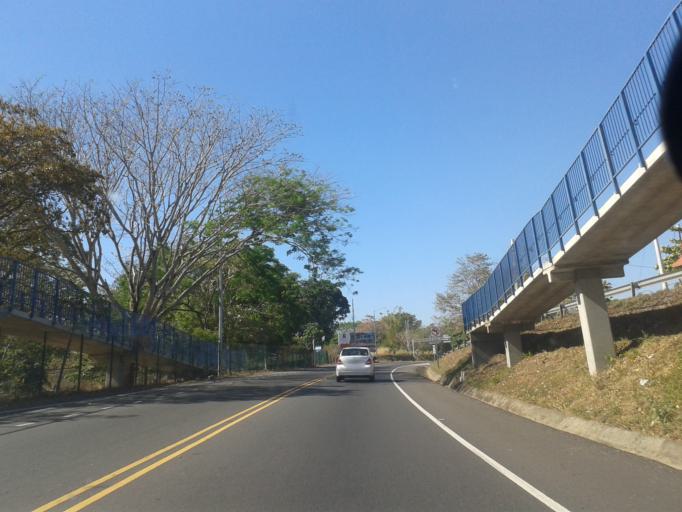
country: CR
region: Alajuela
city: Orotina
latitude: 9.8930
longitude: -84.5605
